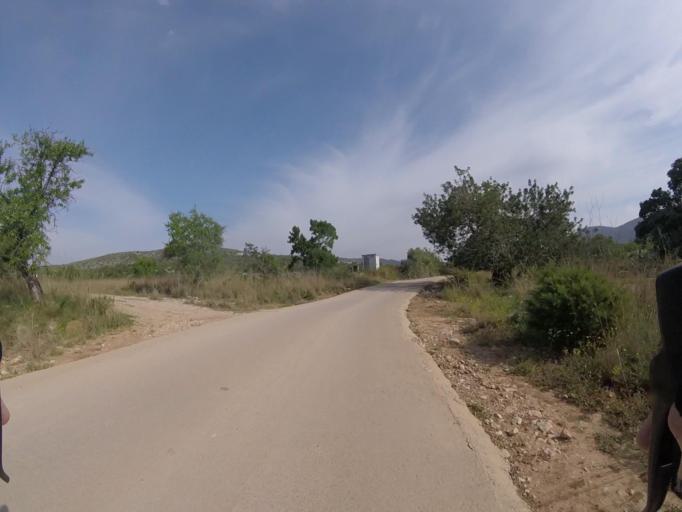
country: ES
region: Valencia
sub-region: Provincia de Castello
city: Alcala de Xivert
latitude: 40.2699
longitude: 0.2525
